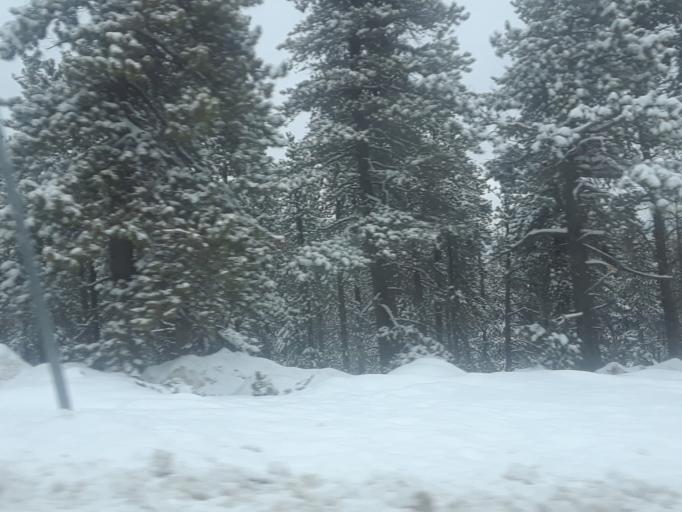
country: US
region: Colorado
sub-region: Boulder County
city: Coal Creek
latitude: 39.9239
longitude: -105.3829
